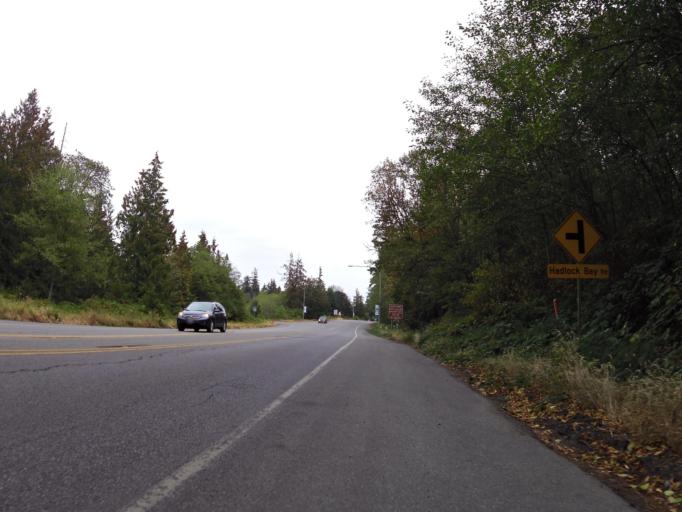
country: US
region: Washington
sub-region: Jefferson County
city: Port Hadlock-Irondale
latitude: 48.0252
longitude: -122.7474
